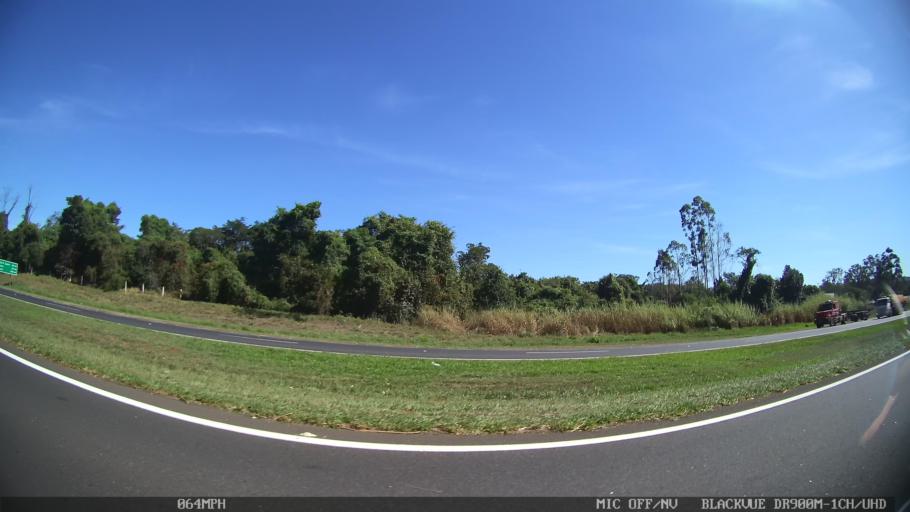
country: BR
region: Sao Paulo
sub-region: Sao Simao
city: Sao Simao
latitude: -21.5424
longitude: -47.6398
